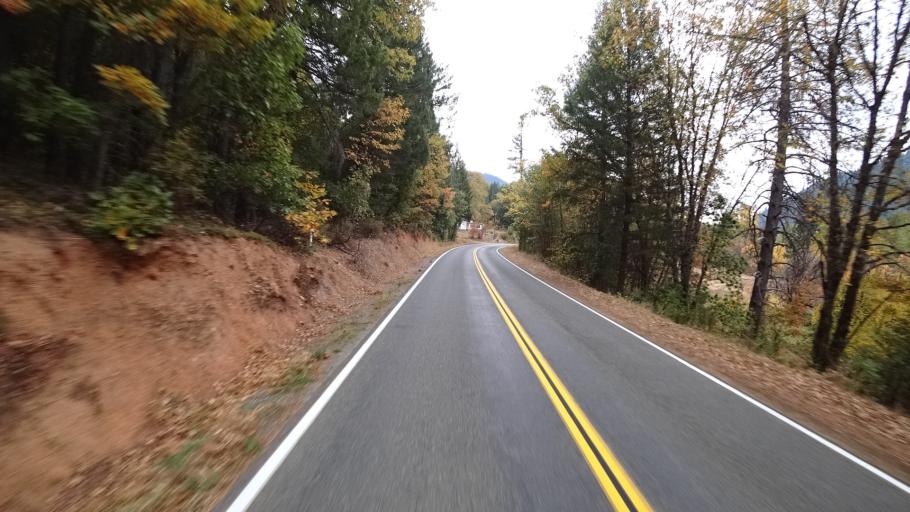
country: US
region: California
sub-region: Siskiyou County
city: Happy Camp
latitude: 41.8829
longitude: -123.4238
